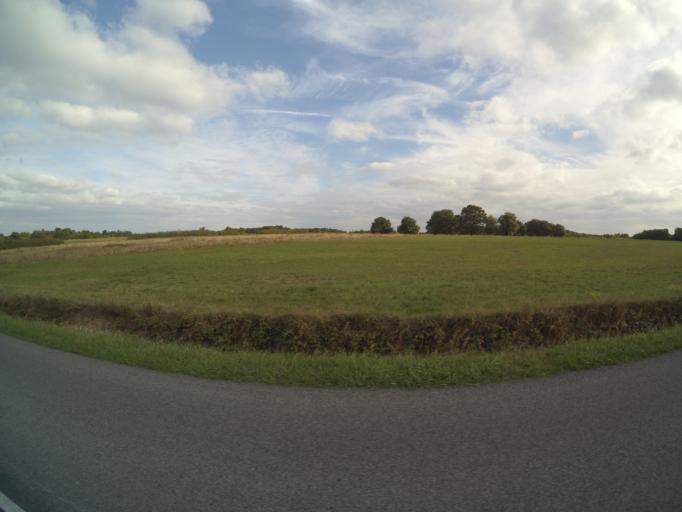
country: FR
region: Centre
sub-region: Departement d'Indre-et-Loire
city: Nazelles-Negron
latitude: 47.4392
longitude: 0.9526
